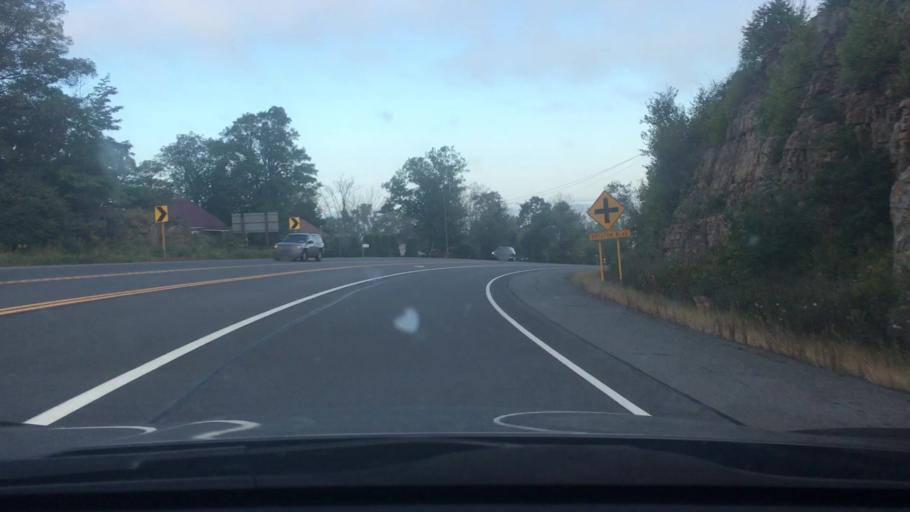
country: US
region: Pennsylvania
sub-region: Luzerne County
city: Hudson
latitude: 41.2266
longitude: -75.8012
